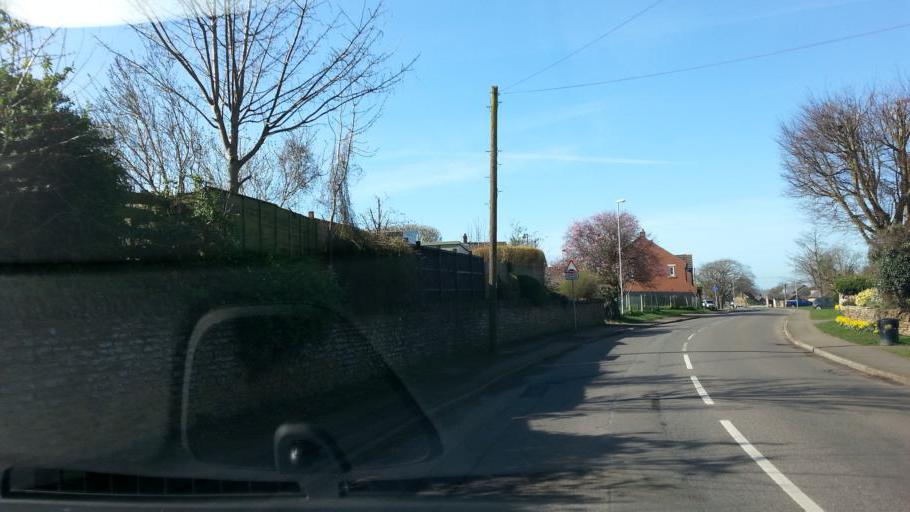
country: GB
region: England
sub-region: Northamptonshire
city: Brixworth
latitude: 52.3293
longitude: -0.8994
